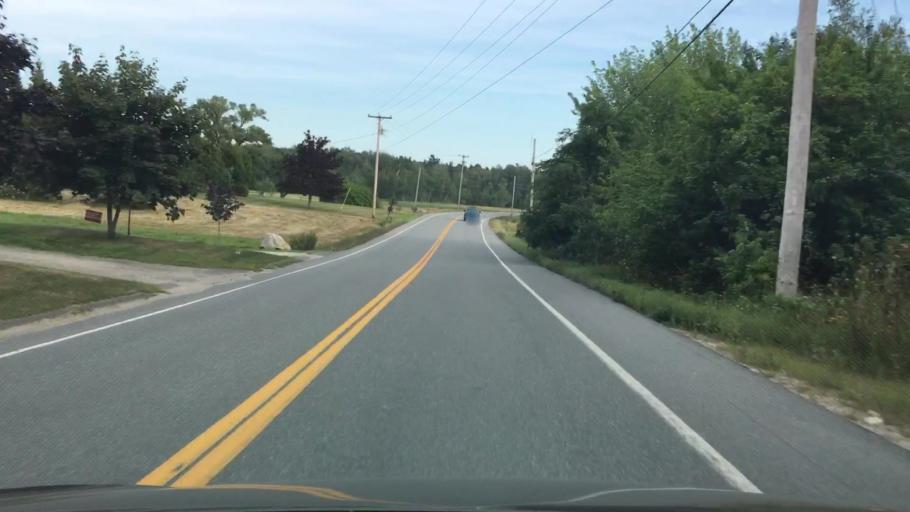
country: US
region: Maine
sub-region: Hancock County
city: Penobscot
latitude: 44.4614
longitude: -68.7821
